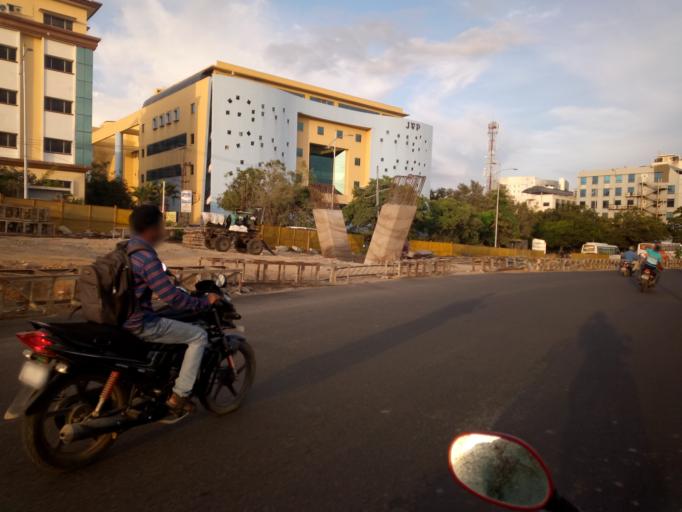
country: IN
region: Telangana
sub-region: Rangareddi
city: Kukatpalli
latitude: 17.4391
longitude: 78.3777
